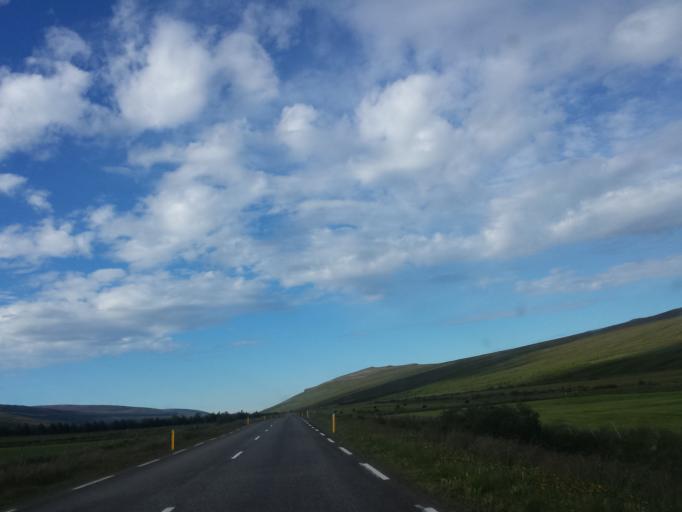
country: IS
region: Northeast
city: Laugar
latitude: 65.7462
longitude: -17.5905
